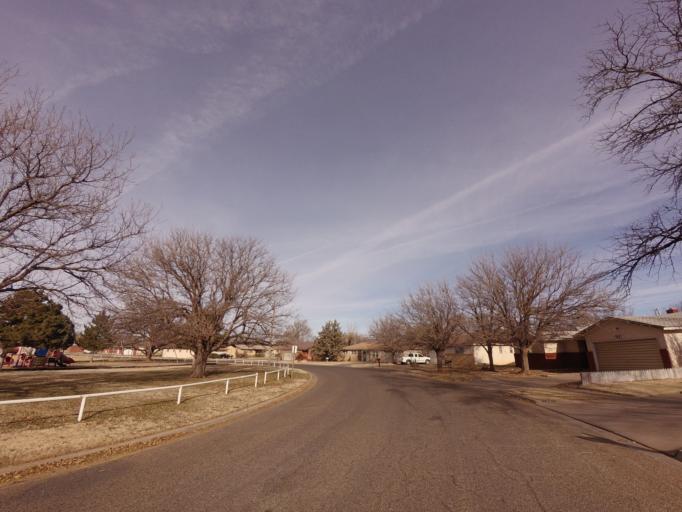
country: US
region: New Mexico
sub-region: Curry County
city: Clovis
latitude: 34.4131
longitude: -103.2174
